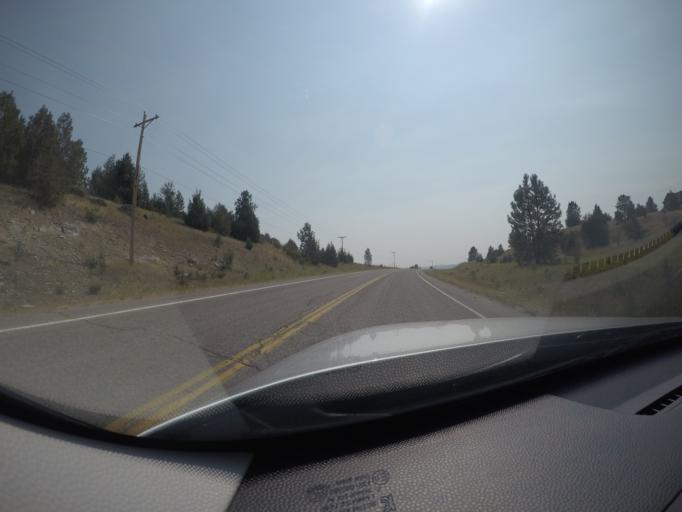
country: US
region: Montana
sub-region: Lake County
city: Polson
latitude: 47.7457
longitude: -114.1730
